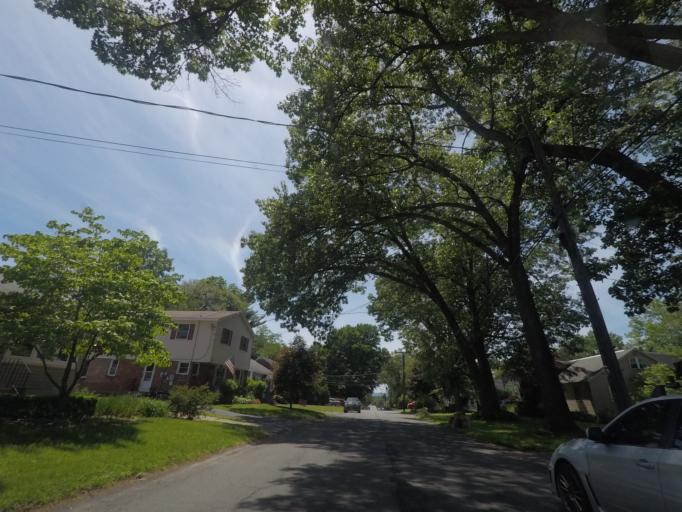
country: US
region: New York
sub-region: Albany County
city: Roessleville
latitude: 42.7002
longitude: -73.8040
